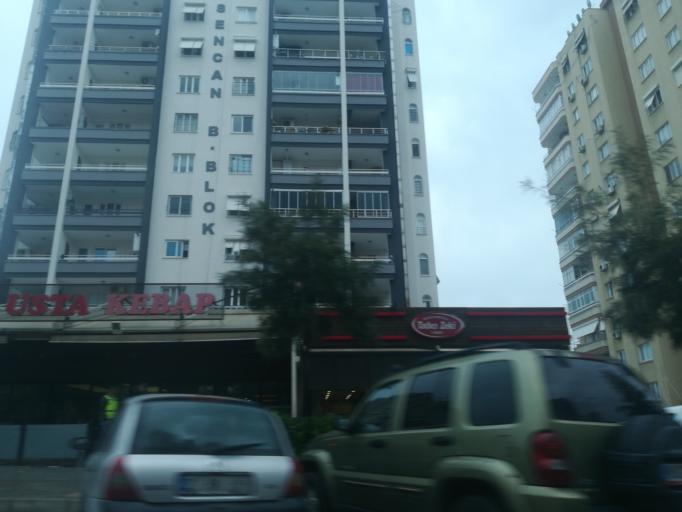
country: TR
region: Adana
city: Adana
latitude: 37.0333
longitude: 35.3087
